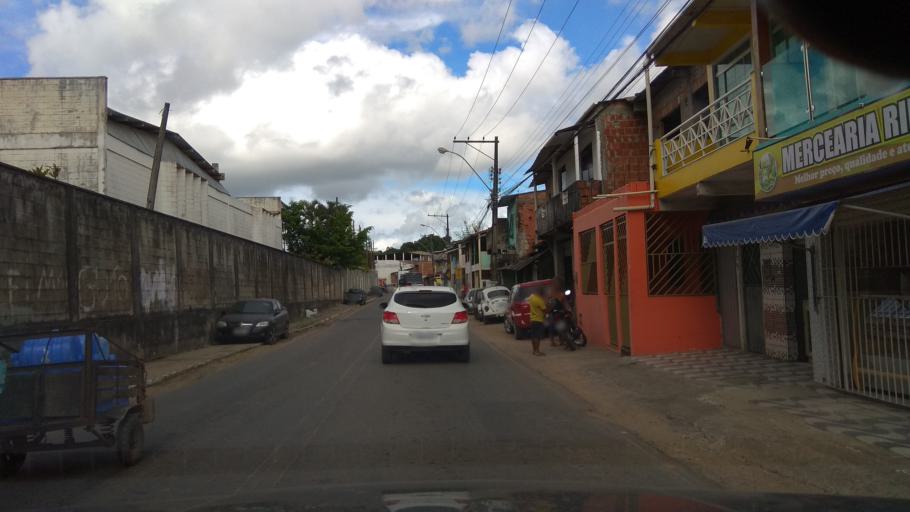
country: BR
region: Bahia
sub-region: Ilheus
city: Ilheus
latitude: -14.7928
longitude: -39.0630
